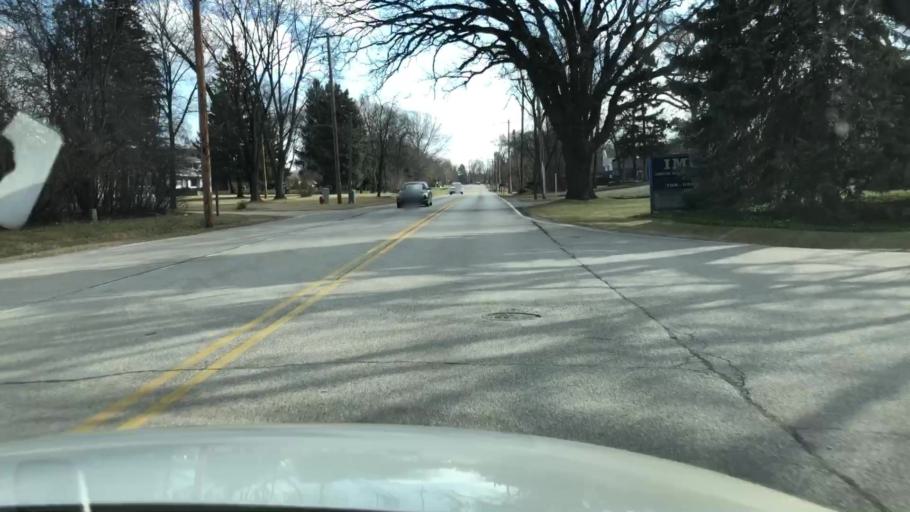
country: US
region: Wisconsin
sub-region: Waukesha County
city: Waukesha
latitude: 43.0430
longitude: -88.1770
